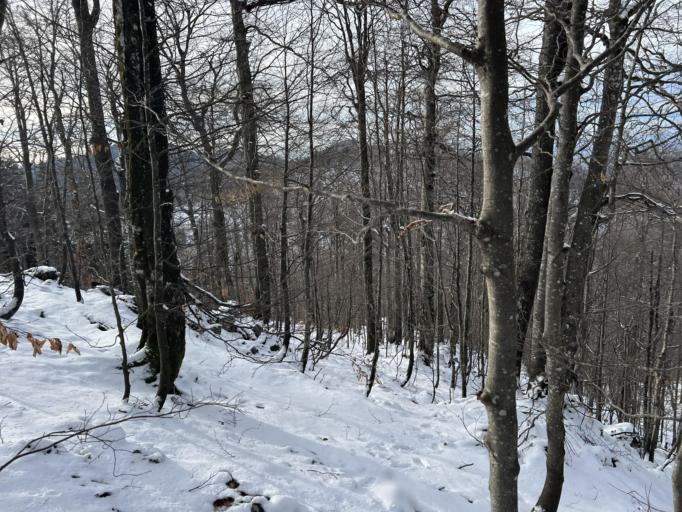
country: SI
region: Ajdovscina
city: Lokavec
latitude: 45.9977
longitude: 13.8422
